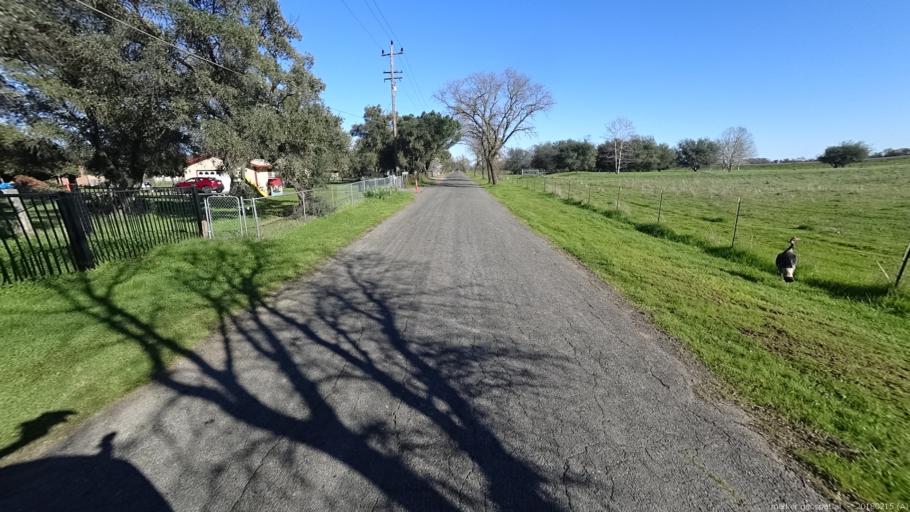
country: US
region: California
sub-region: Sacramento County
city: Rio Linda
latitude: 38.6699
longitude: -121.4739
